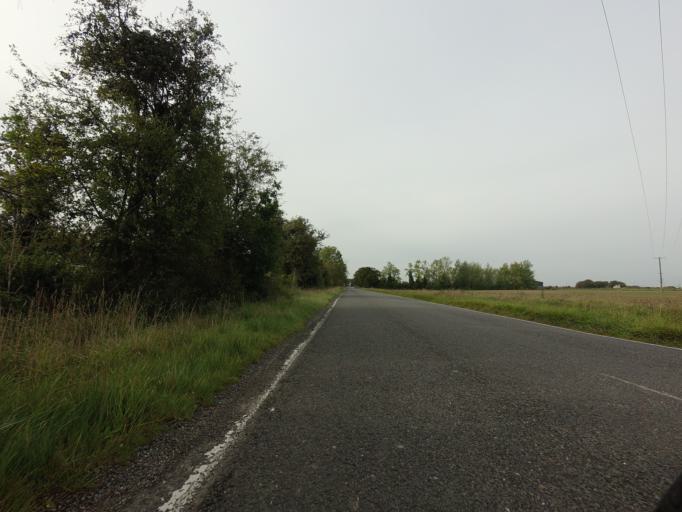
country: GB
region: England
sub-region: Cambridgeshire
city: Melbourn
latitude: 52.0692
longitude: 0.0570
